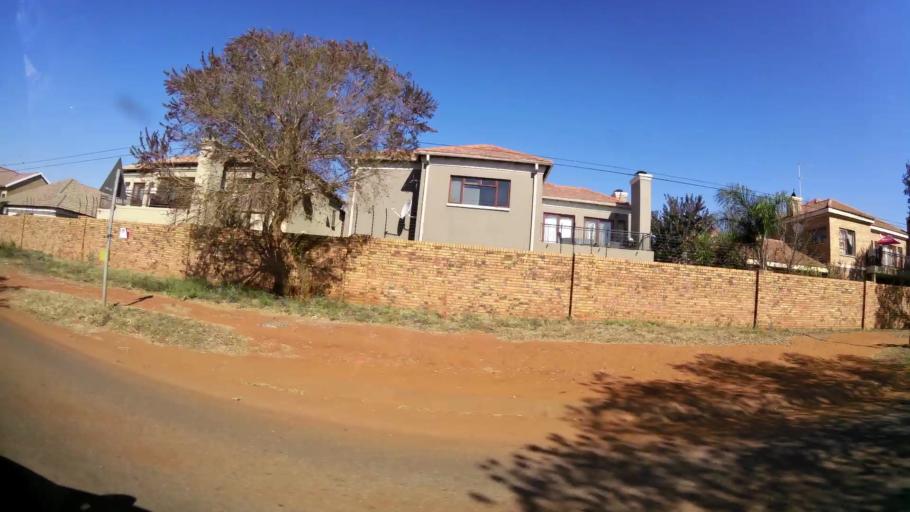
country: ZA
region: Gauteng
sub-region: City of Tshwane Metropolitan Municipality
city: Pretoria
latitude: -25.6614
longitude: 28.2564
